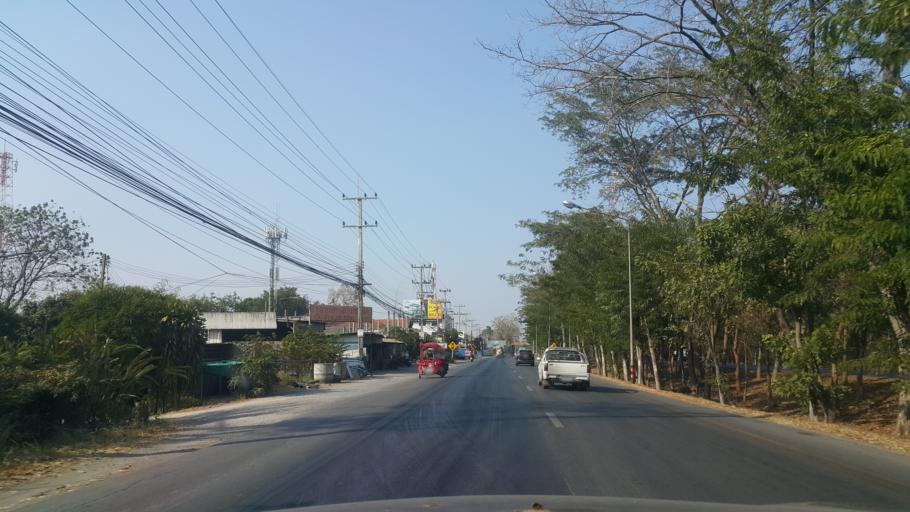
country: TH
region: Nakhon Ratchasima
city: Nakhon Ratchasima
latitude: 14.9046
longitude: 102.0697
